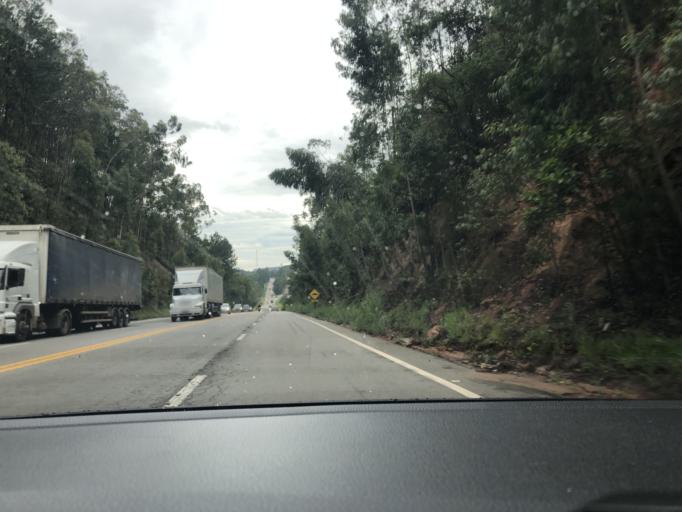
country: BR
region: Sao Paulo
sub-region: Campo Limpo Paulista
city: Campo Limpo Paulista
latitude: -23.1650
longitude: -46.7584
